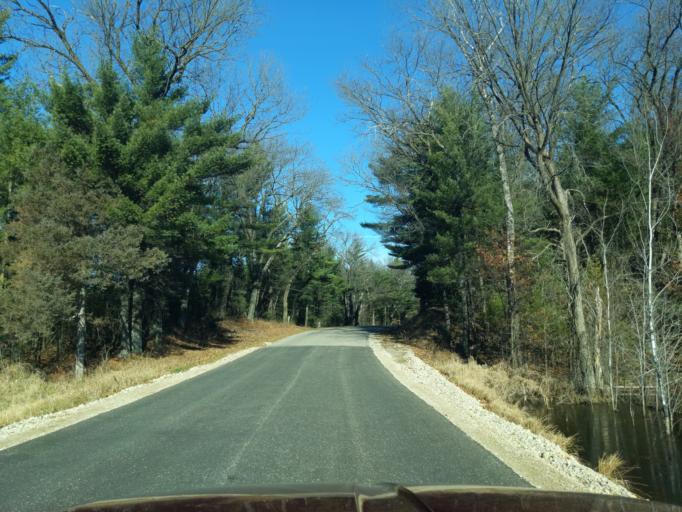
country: US
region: Wisconsin
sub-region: Waushara County
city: Silver Lake
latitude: 44.0848
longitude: -89.1939
